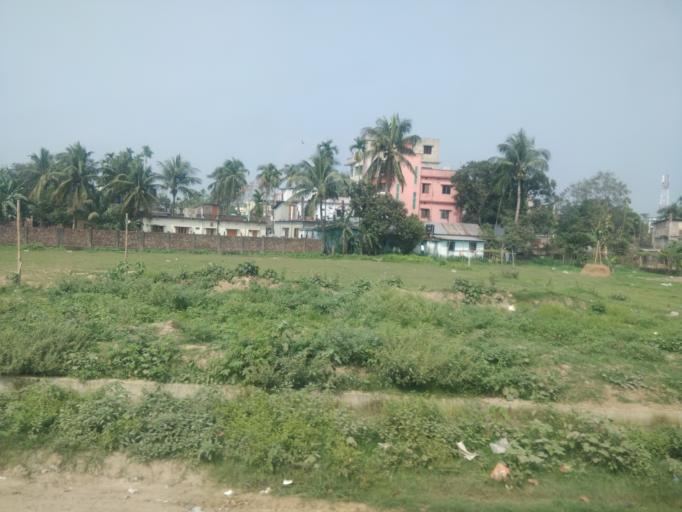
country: BD
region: Sylhet
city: Habiganj
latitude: 24.3666
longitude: 91.4146
